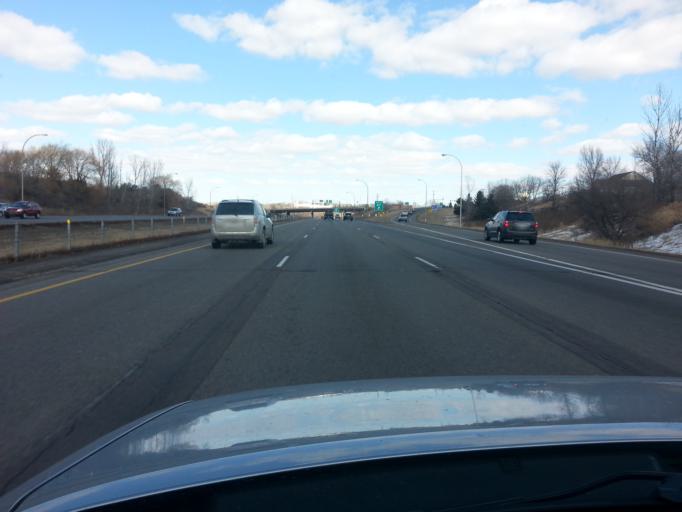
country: US
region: Minnesota
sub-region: Dakota County
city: Inver Grove Heights
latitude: 44.8687
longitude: -93.0846
